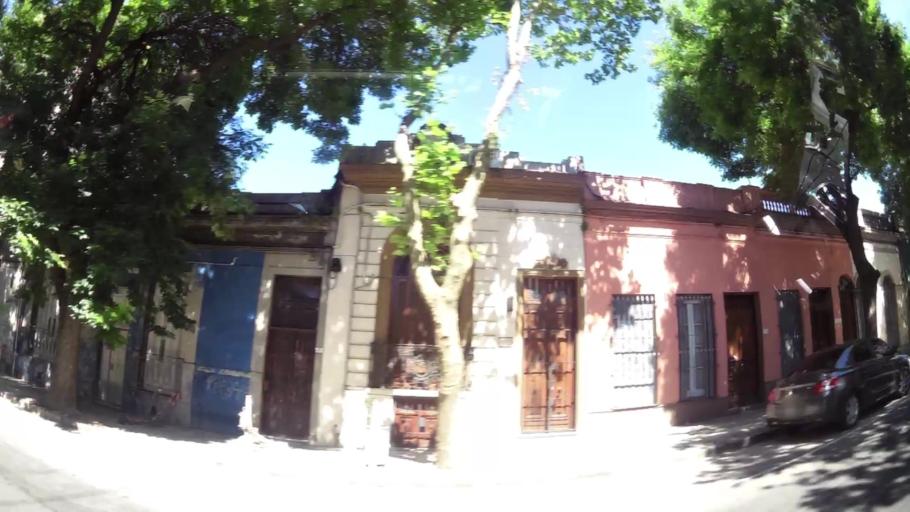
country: UY
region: Montevideo
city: Montevideo
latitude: -34.9100
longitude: -56.1865
